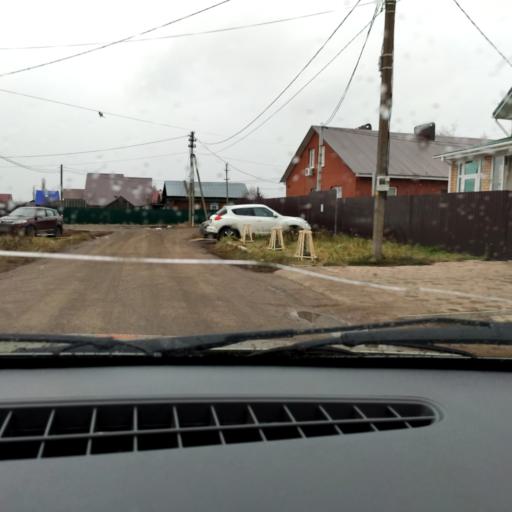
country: RU
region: Bashkortostan
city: Ufa
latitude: 54.6098
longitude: 55.9477
